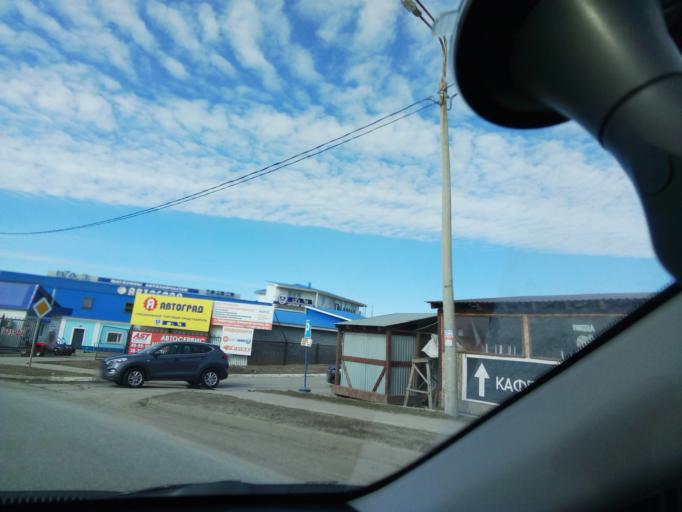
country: RU
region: Chuvashia
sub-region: Cheboksarskiy Rayon
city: Cheboksary
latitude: 56.1024
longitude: 47.2529
